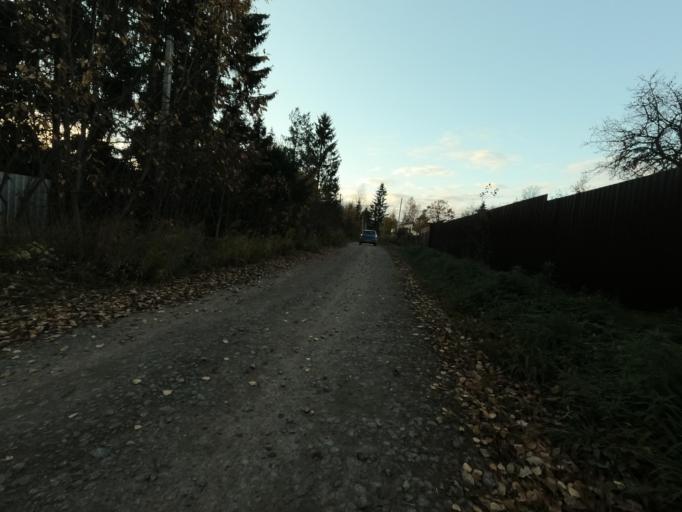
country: RU
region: Leningrad
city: Mga
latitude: 59.7819
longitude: 31.1994
